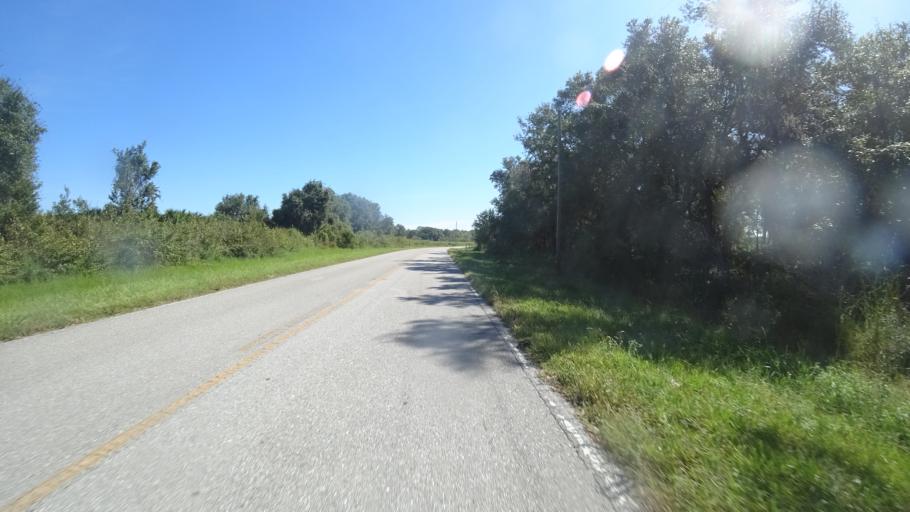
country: US
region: Florida
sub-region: DeSoto County
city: Nocatee
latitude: 27.2736
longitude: -82.1103
